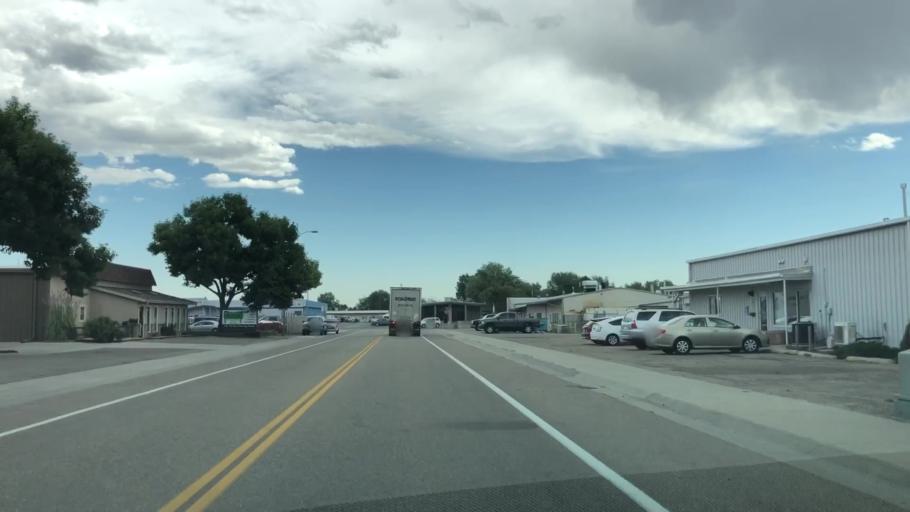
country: US
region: Colorado
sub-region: Larimer County
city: Fort Collins
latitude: 40.5834
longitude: -105.0519
